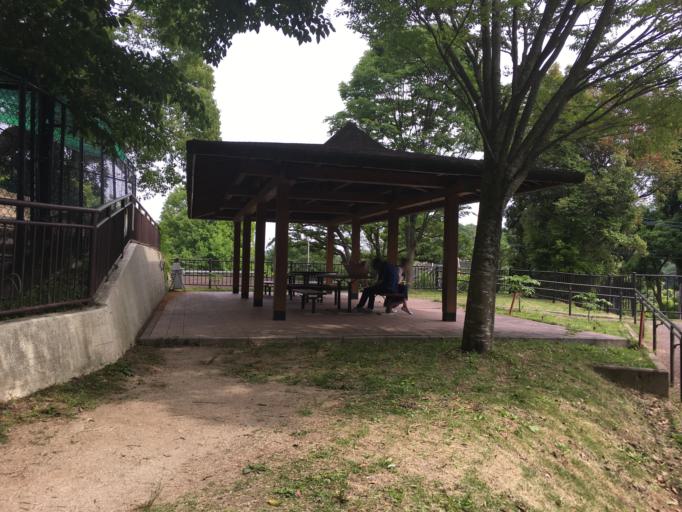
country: JP
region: Fukuoka
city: Fukuoka-shi
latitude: 33.5742
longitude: 130.3903
